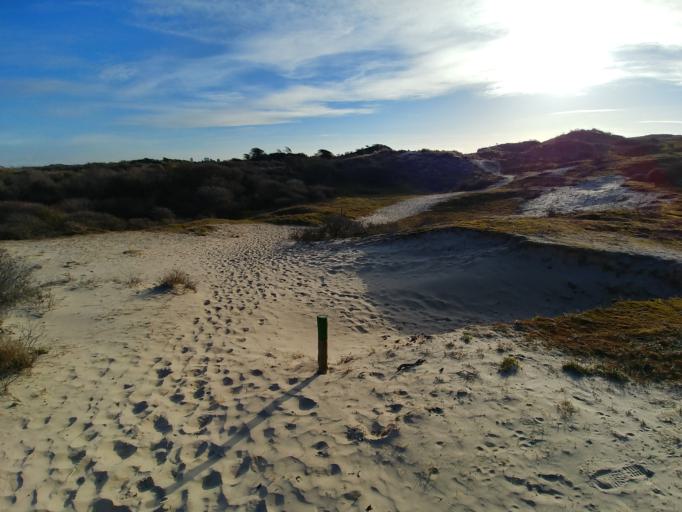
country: NL
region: South Holland
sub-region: Gemeente Den Haag
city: Scheveningen
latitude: 52.1317
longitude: 4.3137
